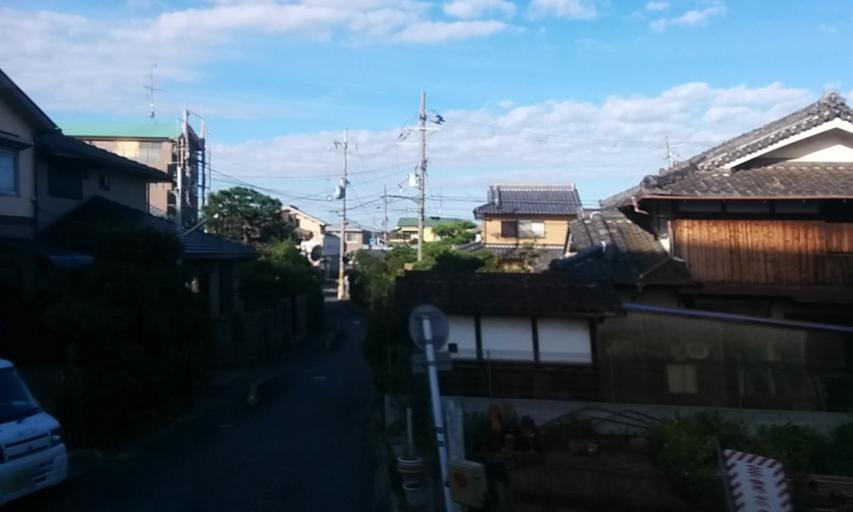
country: JP
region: Kyoto
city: Tanabe
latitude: 34.8548
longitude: 135.7724
